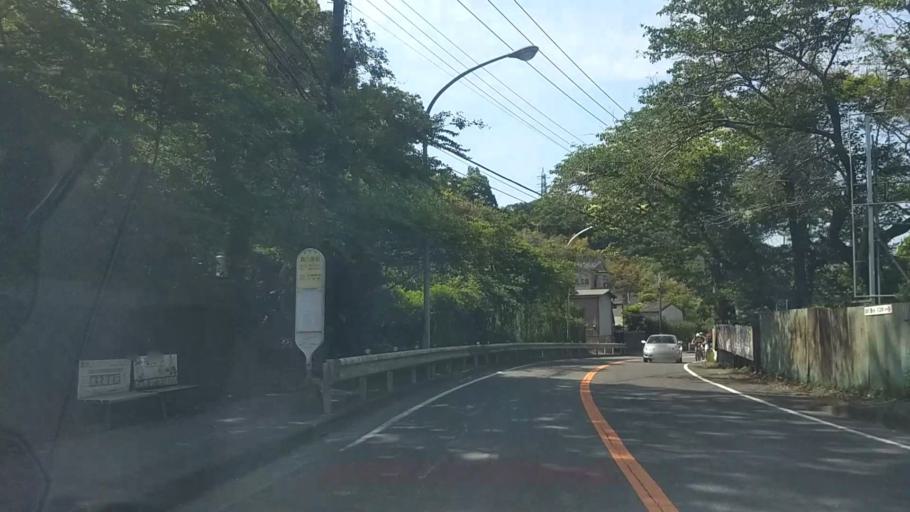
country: JP
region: Kanagawa
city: Kamakura
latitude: 35.3410
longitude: 139.5825
